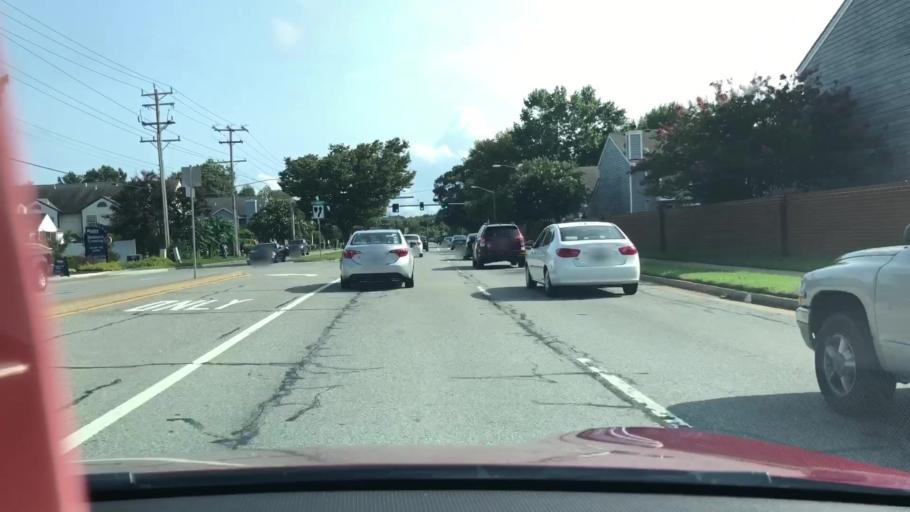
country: US
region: Virginia
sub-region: City of Virginia Beach
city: Virginia Beach
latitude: 36.8514
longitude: -75.9944
